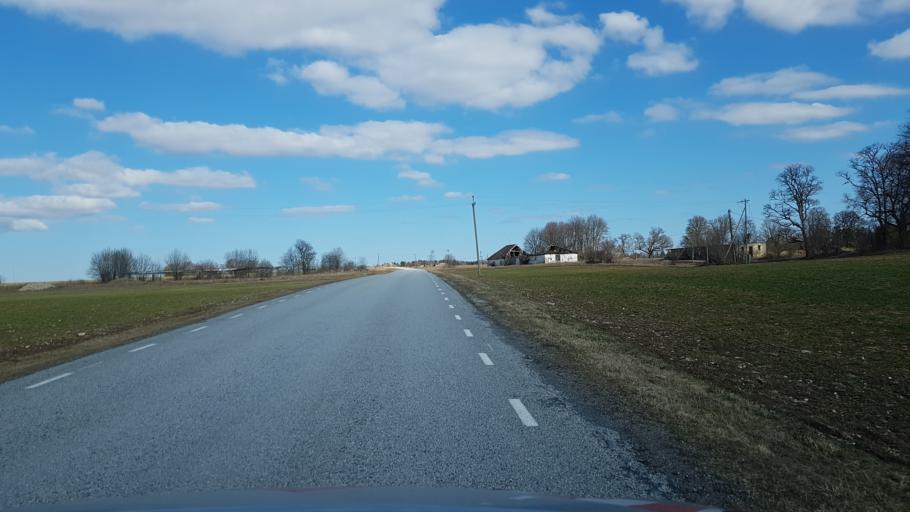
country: EE
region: Laeaene-Virumaa
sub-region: Kadrina vald
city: Kadrina
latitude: 59.2901
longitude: 26.1863
